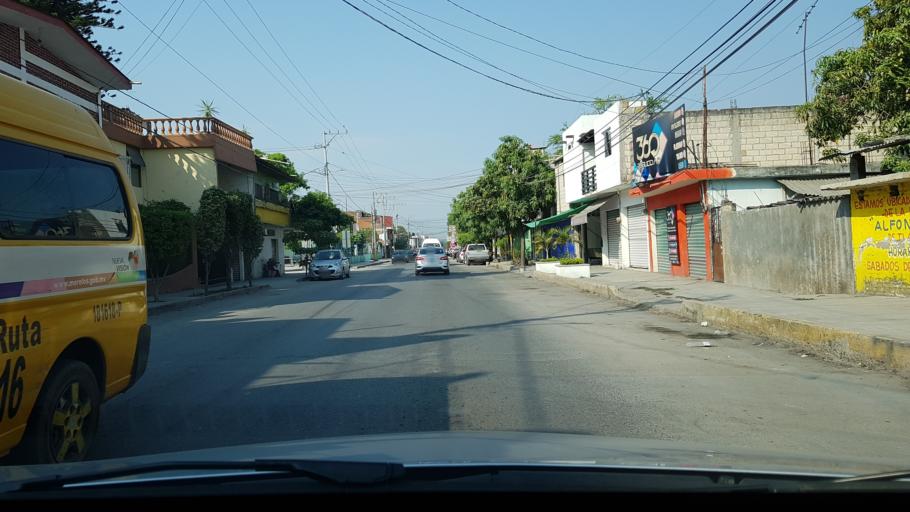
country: MX
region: Morelos
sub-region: Jojutla
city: Jojutla
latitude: 18.6200
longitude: -99.1727
